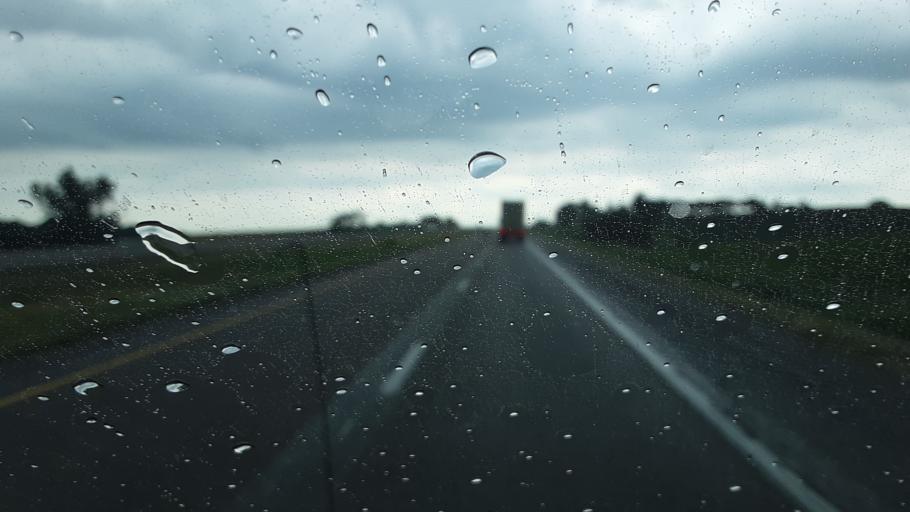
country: US
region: Iowa
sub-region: Pottawattamie County
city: Council Bluffs
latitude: 41.3184
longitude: -95.7552
